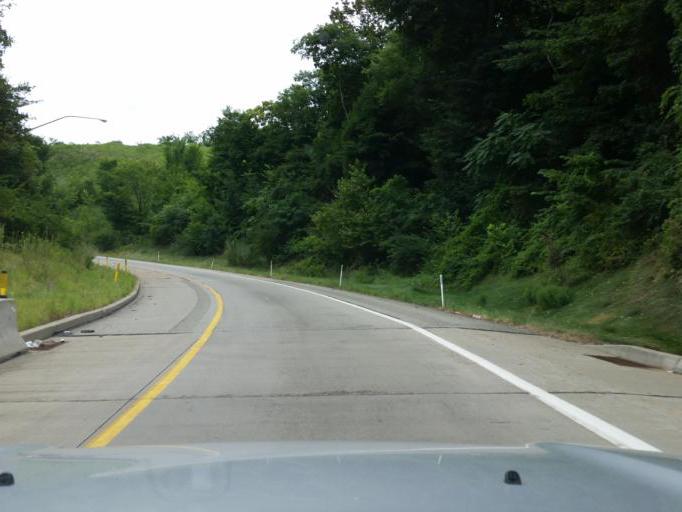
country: US
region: Pennsylvania
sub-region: Allegheny County
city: Edgewood
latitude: 40.4322
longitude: -79.8712
